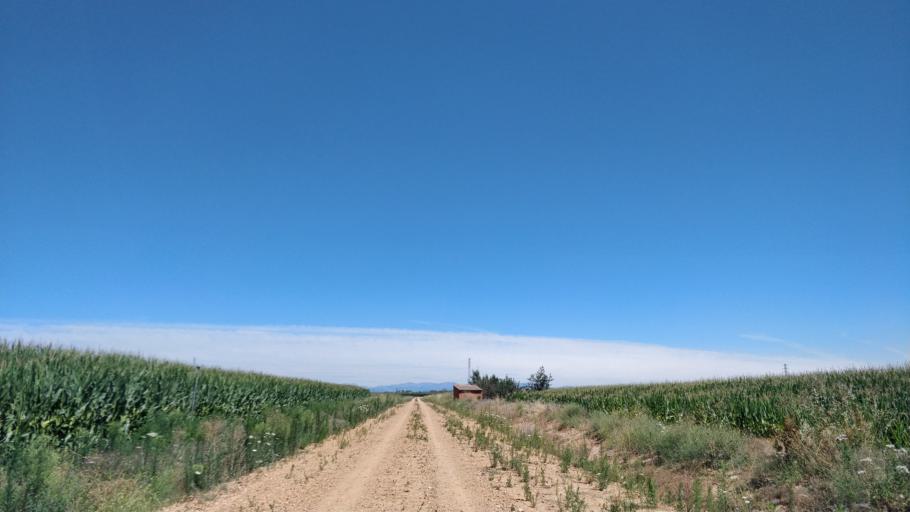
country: ES
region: Castille and Leon
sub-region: Provincia de Leon
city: Bustillo del Paramo
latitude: 42.4565
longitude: -5.8166
